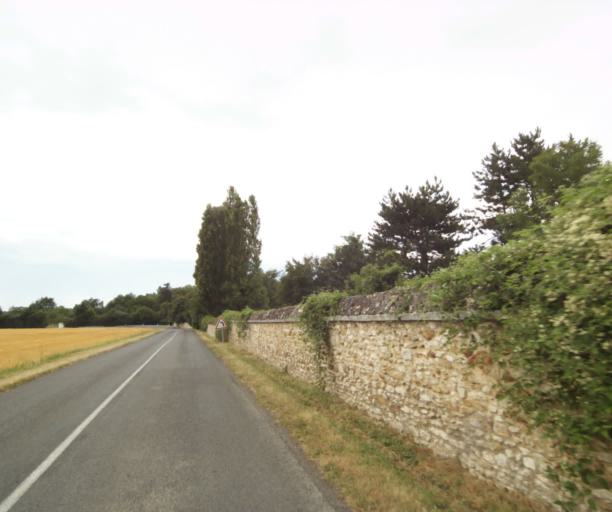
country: FR
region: Ile-de-France
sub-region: Departement de Seine-et-Marne
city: Cely
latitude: 48.4697
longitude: 2.5220
